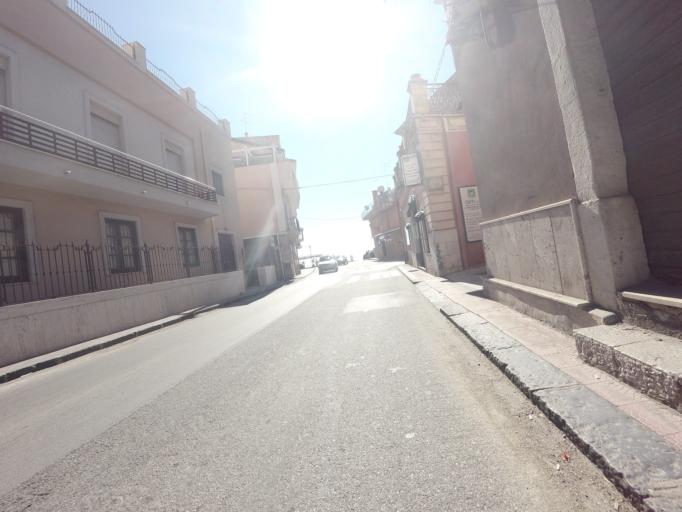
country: IT
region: Sicily
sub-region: Messina
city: Taormina
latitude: 37.8427
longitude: 15.2799
